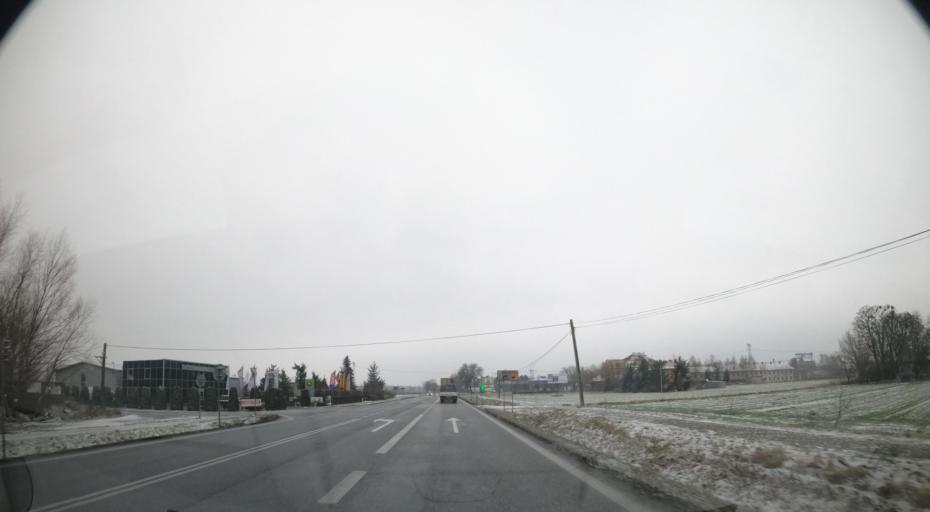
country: PL
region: Masovian Voivodeship
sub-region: Powiat warszawski zachodni
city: Bieniewice
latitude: 52.2040
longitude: 20.5163
